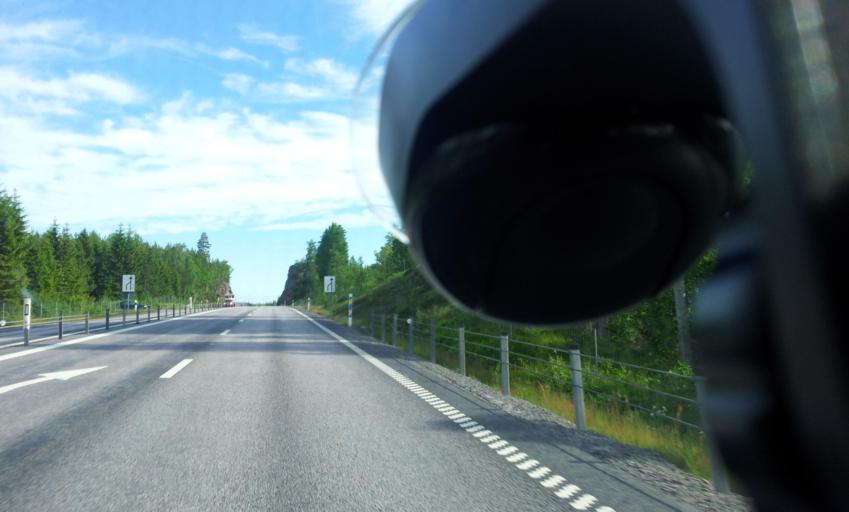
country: SE
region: OEstergoetland
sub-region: Valdemarsviks Kommun
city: Gusum
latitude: 58.2932
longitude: 16.4956
